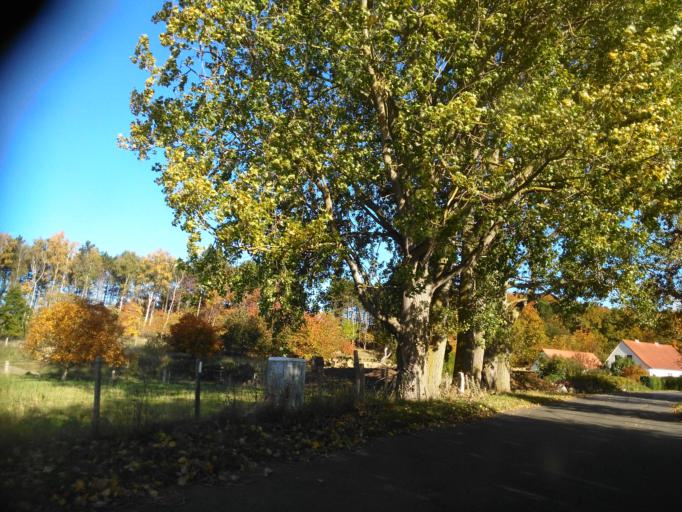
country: DE
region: Mecklenburg-Vorpommern
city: Rambin
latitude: 54.2989
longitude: 13.1972
